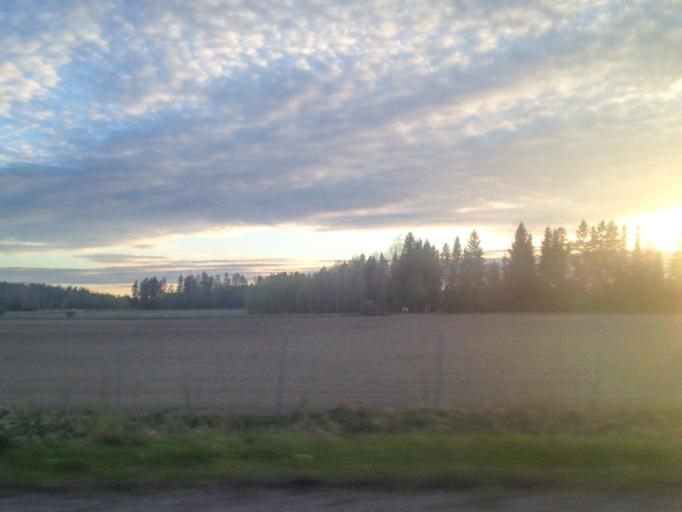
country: FI
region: Uusimaa
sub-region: Helsinki
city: Hyvinge
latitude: 60.6005
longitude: 24.7987
